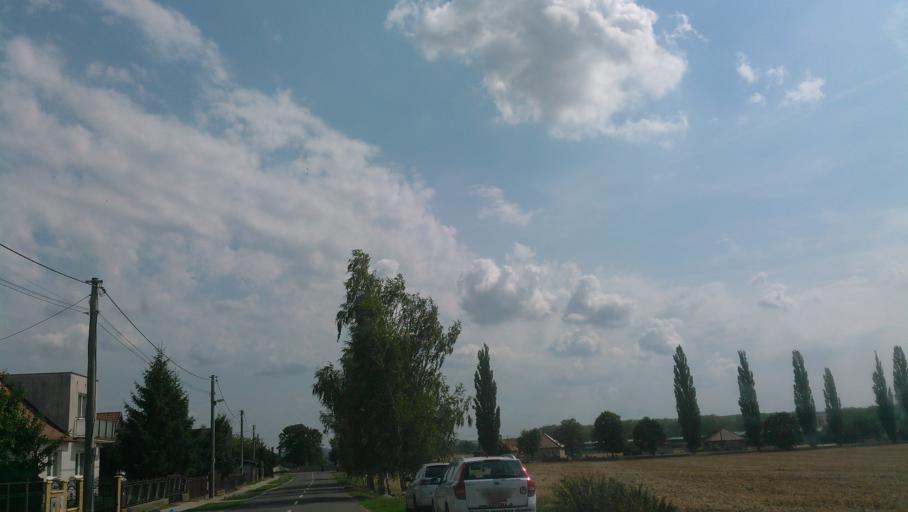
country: SK
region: Nitriansky
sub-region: Okres Nitra
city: Nitra
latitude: 48.3736
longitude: 18.0309
